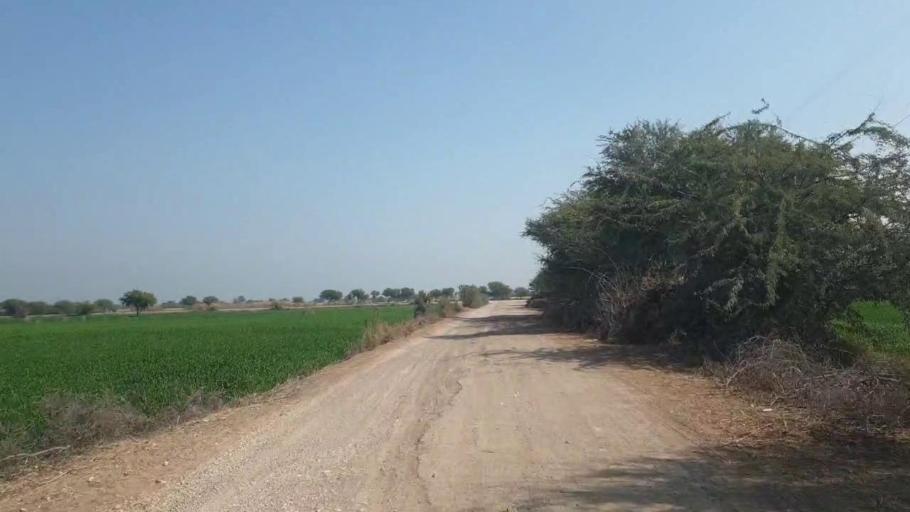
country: PK
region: Sindh
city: Shahdadpur
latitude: 26.0529
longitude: 68.4776
